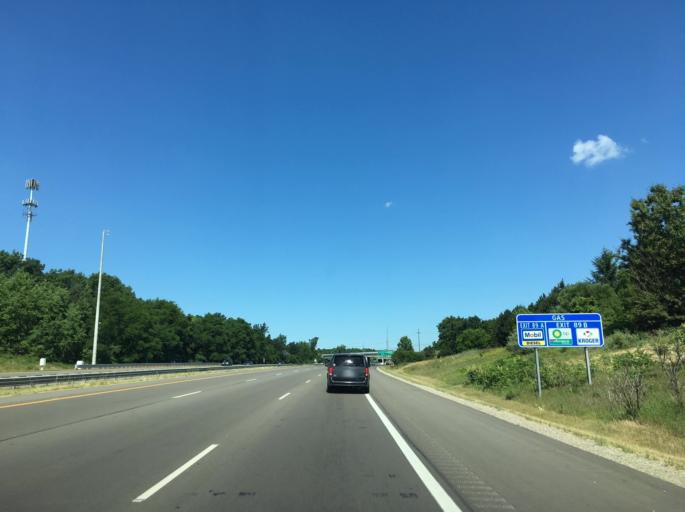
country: US
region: Michigan
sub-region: Oakland County
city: Clarkston
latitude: 42.7319
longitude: -83.3723
